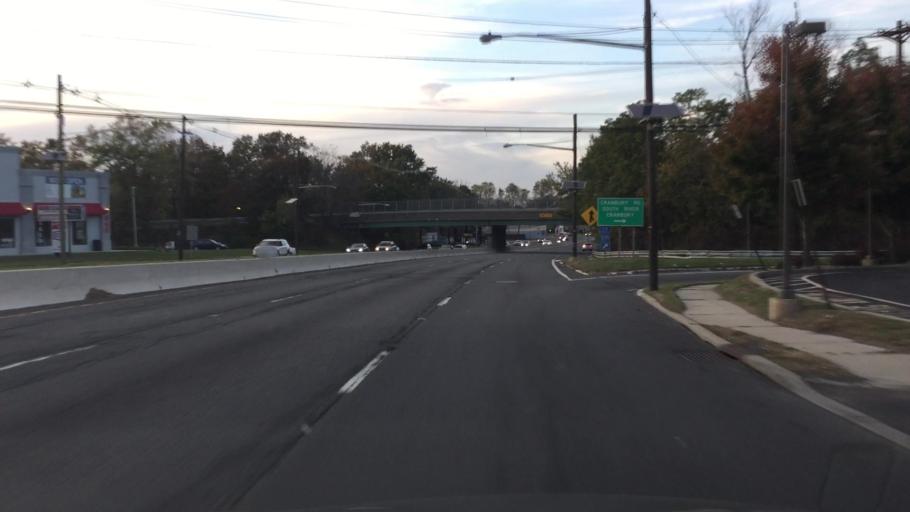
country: US
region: New Jersey
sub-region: Middlesex County
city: South River
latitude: 40.4385
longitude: -74.3925
